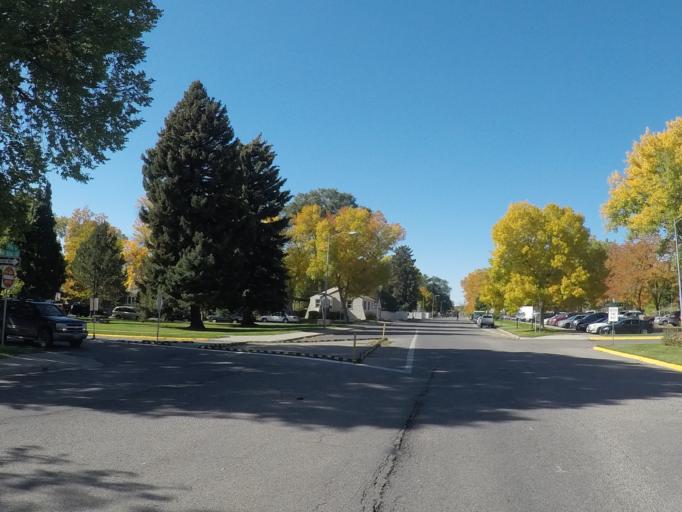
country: US
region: Montana
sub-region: Yellowstone County
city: Billings
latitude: 45.7950
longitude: -108.5215
